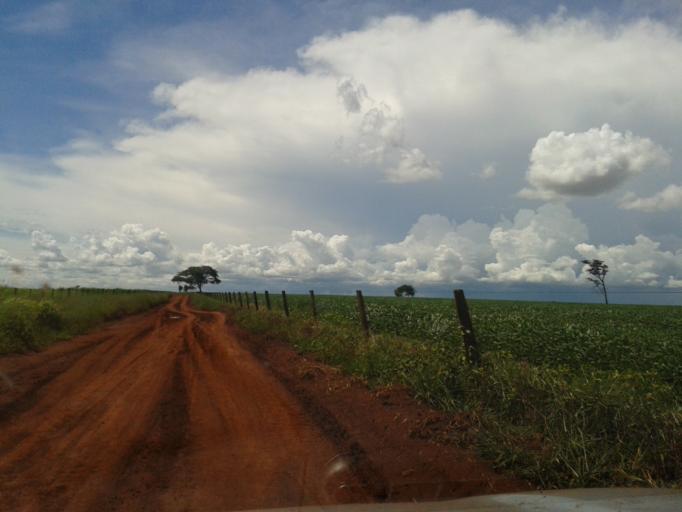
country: BR
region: Minas Gerais
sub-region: Capinopolis
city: Capinopolis
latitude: -18.7511
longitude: -49.7820
